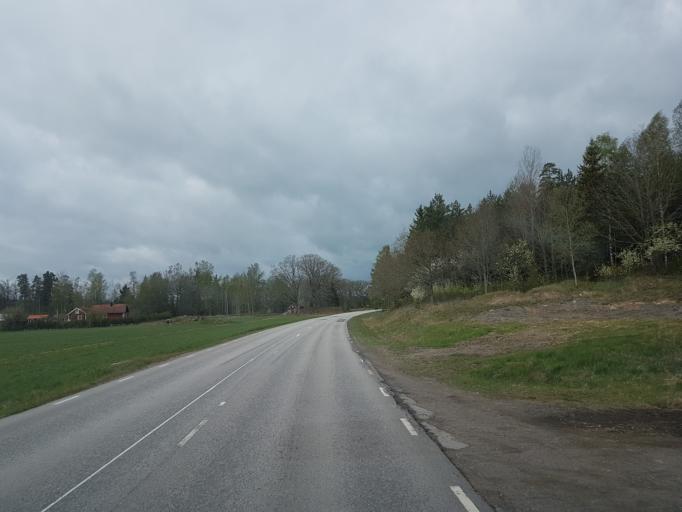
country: SE
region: OEstergoetland
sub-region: Linkopings Kommun
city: Linghem
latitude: 58.4028
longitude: 15.8155
